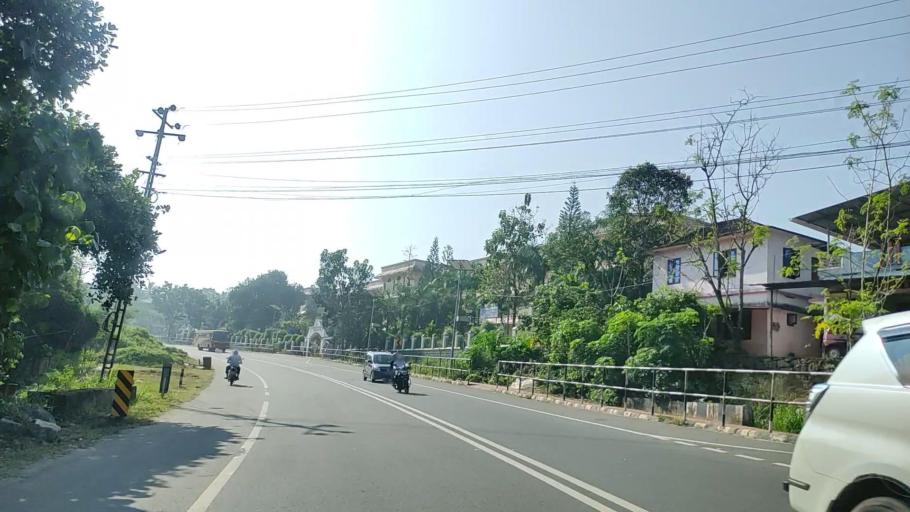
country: IN
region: Kerala
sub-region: Kollam
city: Punalur
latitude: 8.8890
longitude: 76.8674
